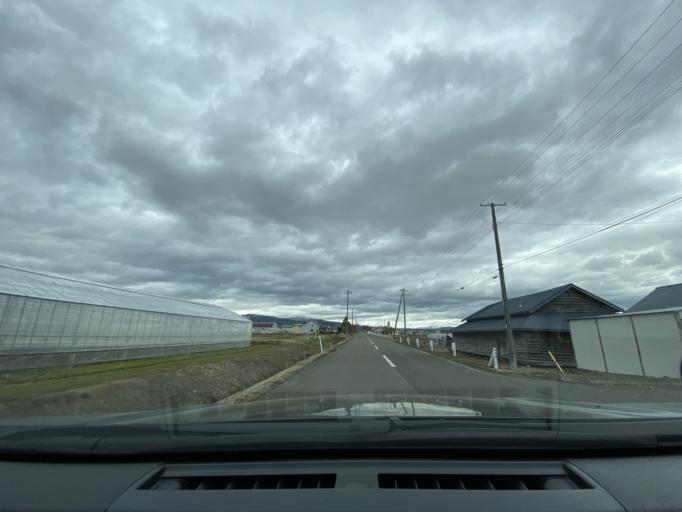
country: JP
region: Hokkaido
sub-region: Asahikawa-shi
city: Asahikawa
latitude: 43.8654
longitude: 142.4721
